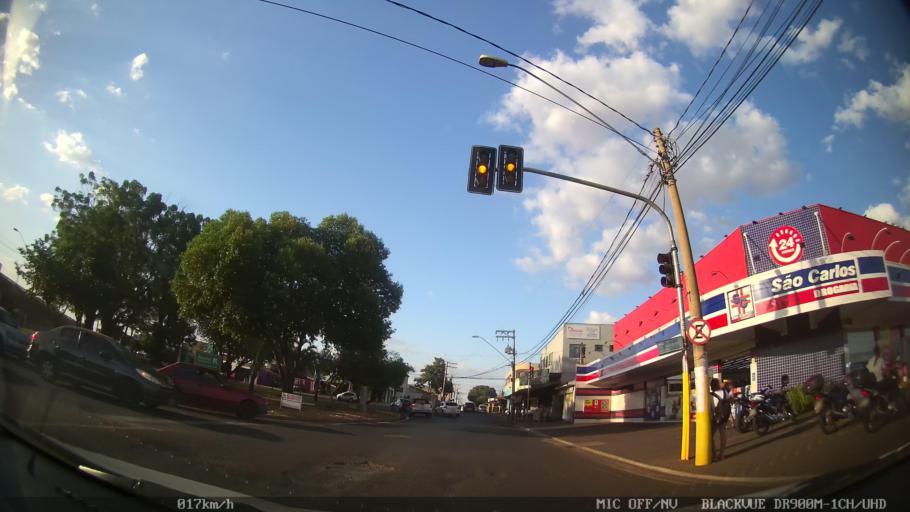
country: BR
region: Sao Paulo
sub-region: Ribeirao Preto
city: Ribeirao Preto
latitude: -21.1888
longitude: -47.7568
